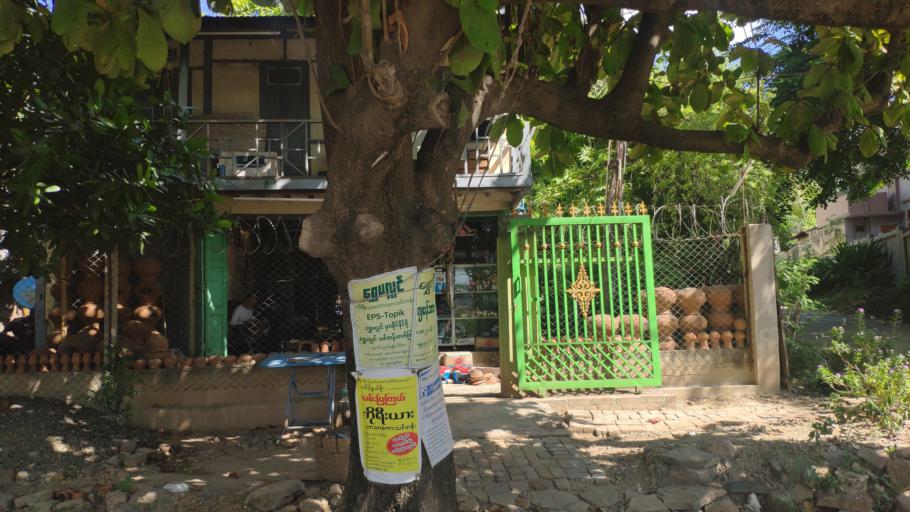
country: MM
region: Mandalay
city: Meiktila
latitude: 20.8982
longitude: 95.8563
